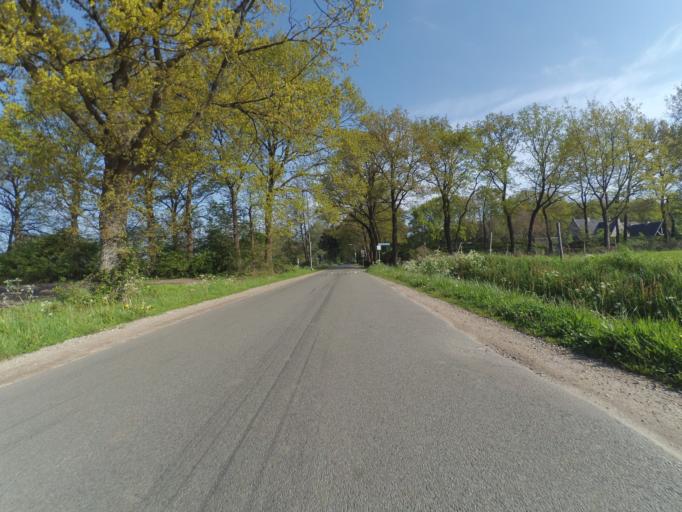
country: NL
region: Gelderland
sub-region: Gemeente Barneveld
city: Voorthuizen
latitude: 52.1796
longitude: 5.6142
